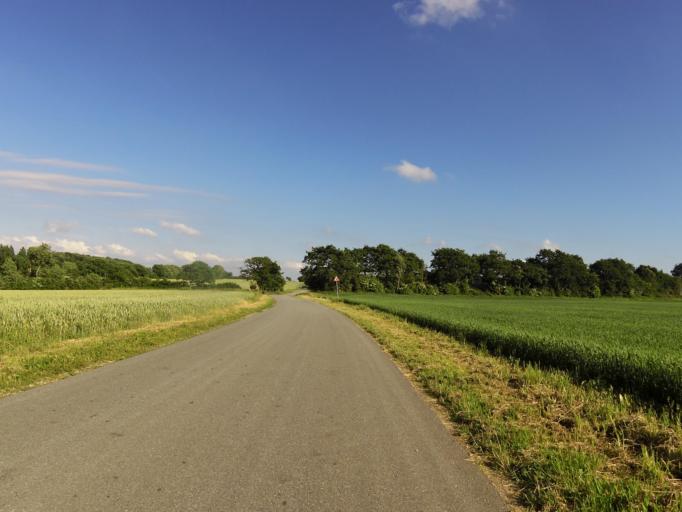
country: DK
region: South Denmark
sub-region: Vejen Kommune
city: Rodding
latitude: 55.3582
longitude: 9.0717
